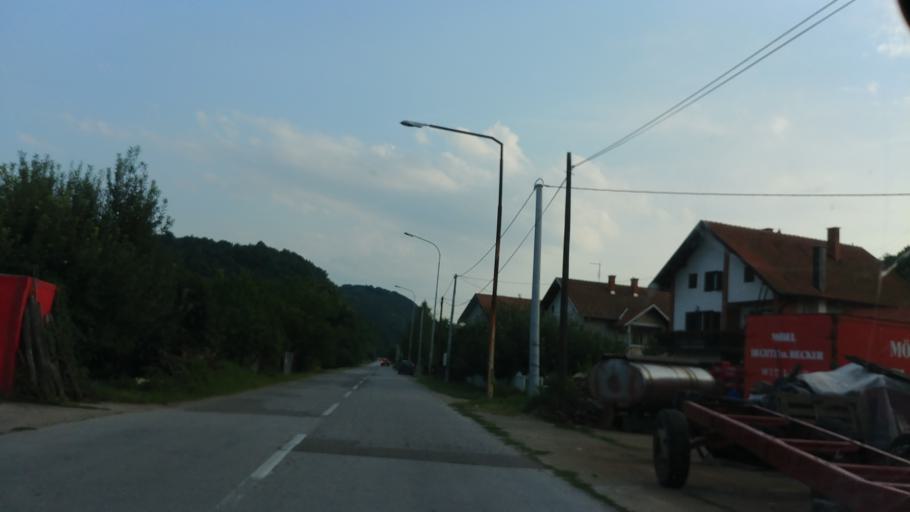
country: BA
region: Republika Srpska
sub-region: Opstina Ugljevik
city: Ugljevik
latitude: 44.6929
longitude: 19.0137
